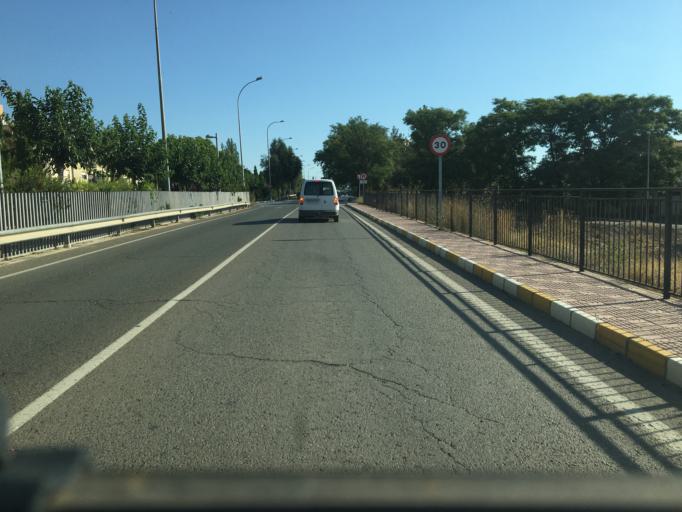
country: ES
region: Murcia
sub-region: Murcia
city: Puerto Lumbreras
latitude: 37.5572
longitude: -1.8097
